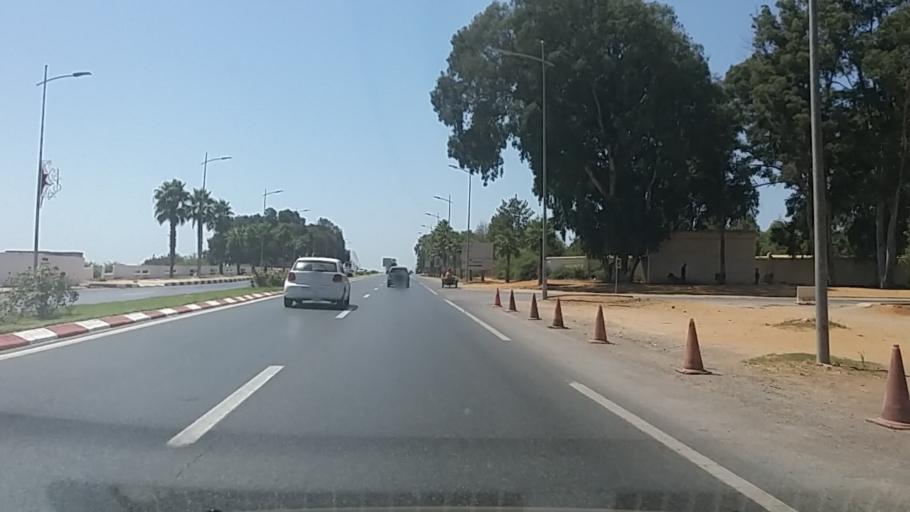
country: MA
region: Rabat-Sale-Zemmour-Zaer
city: Sale
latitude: 34.0305
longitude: -6.7496
